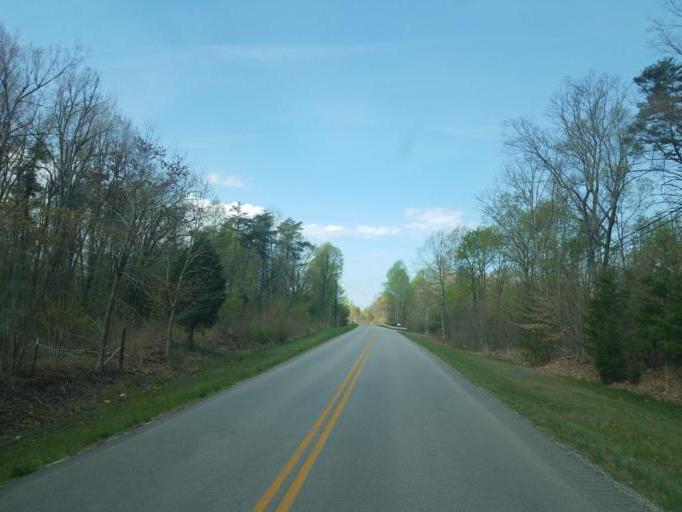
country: US
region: Kentucky
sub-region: Edmonson County
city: Brownsville
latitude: 37.2736
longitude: -86.2145
